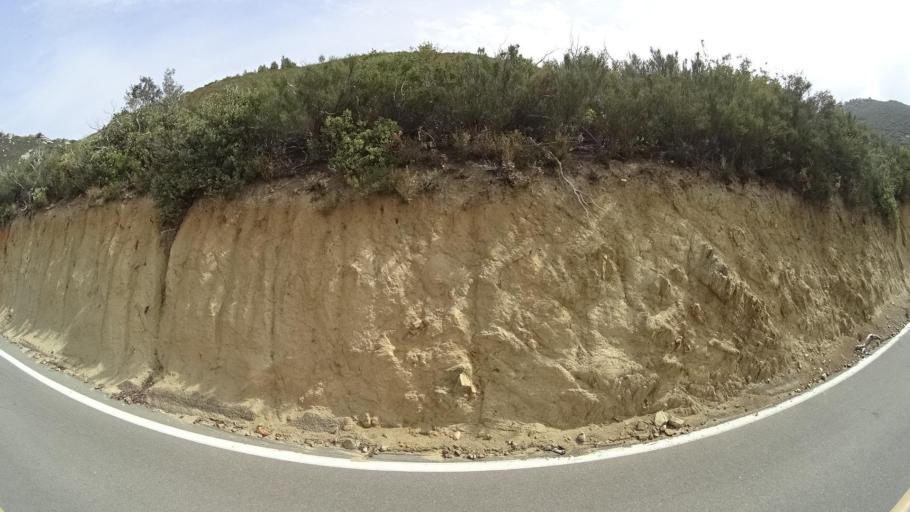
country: US
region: California
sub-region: San Diego County
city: Descanso
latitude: 32.9177
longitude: -116.6335
